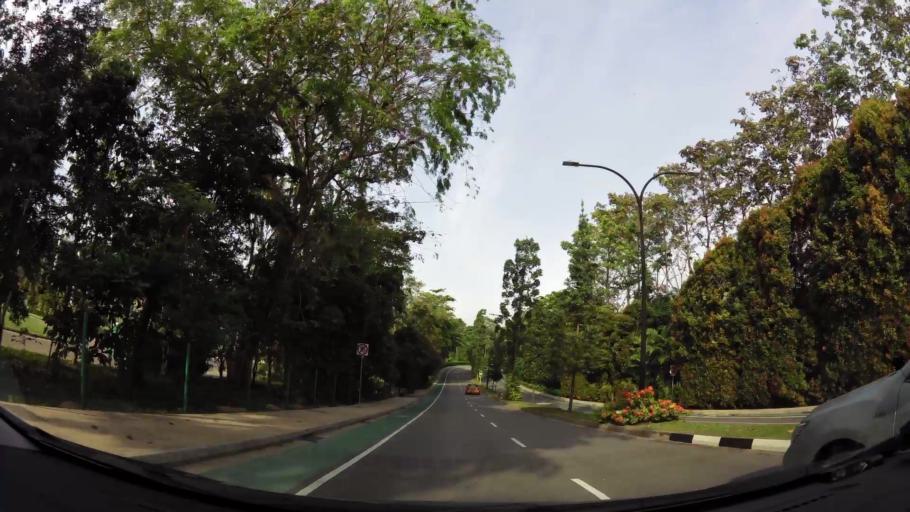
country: SG
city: Singapore
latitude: 1.2480
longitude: 103.8305
